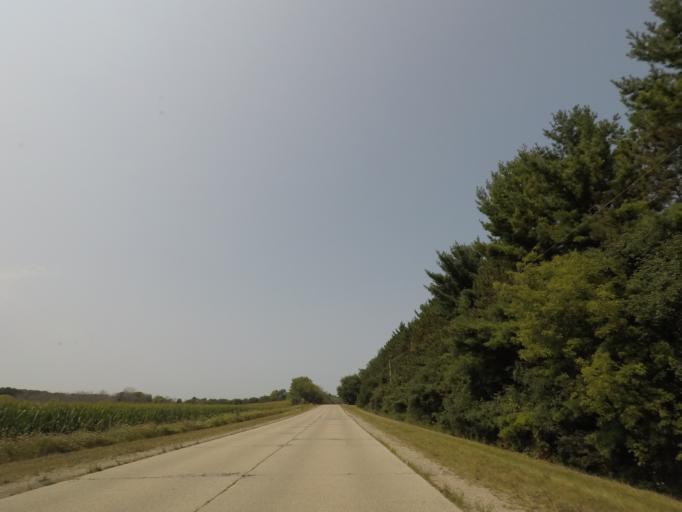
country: US
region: Wisconsin
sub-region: Waukesha County
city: Oconomowoc
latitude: 43.0611
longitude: -88.5263
